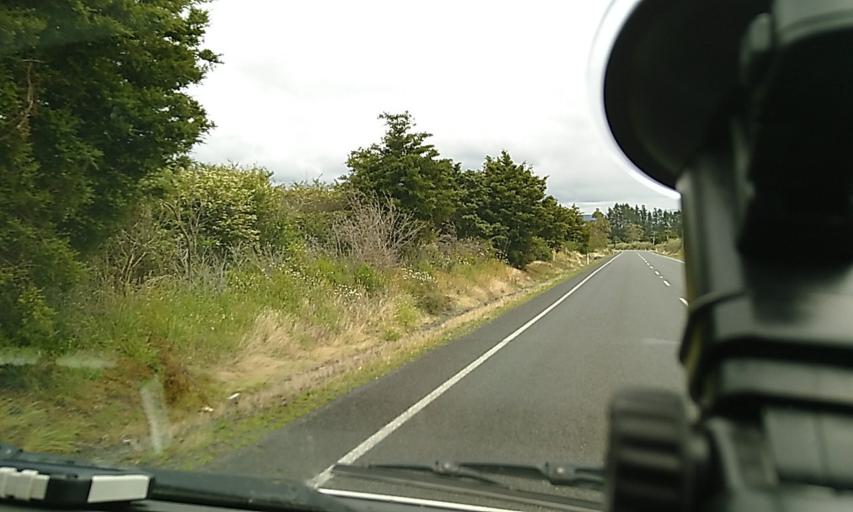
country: NZ
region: Northland
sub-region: Far North District
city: Waimate North
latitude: -35.4374
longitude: 173.7601
